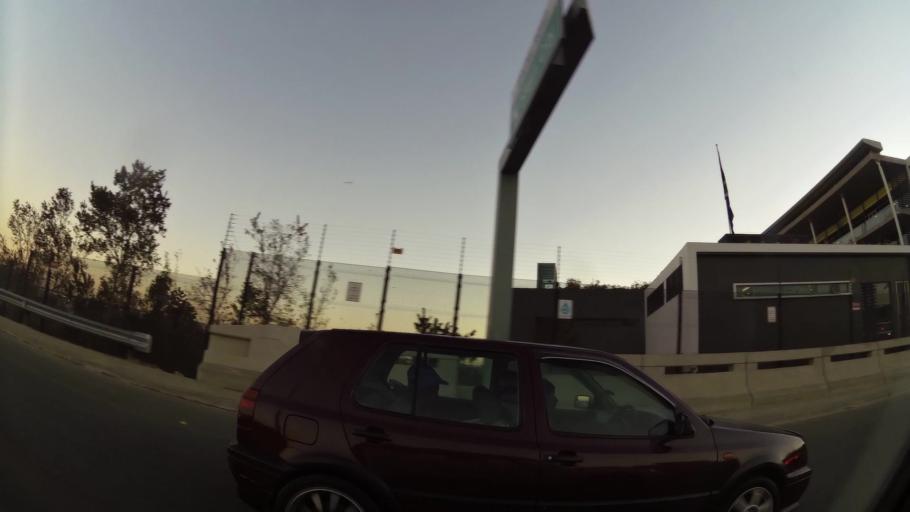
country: ZA
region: Gauteng
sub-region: City of Johannesburg Metropolitan Municipality
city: Diepsloot
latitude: -25.9798
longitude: 28.0149
